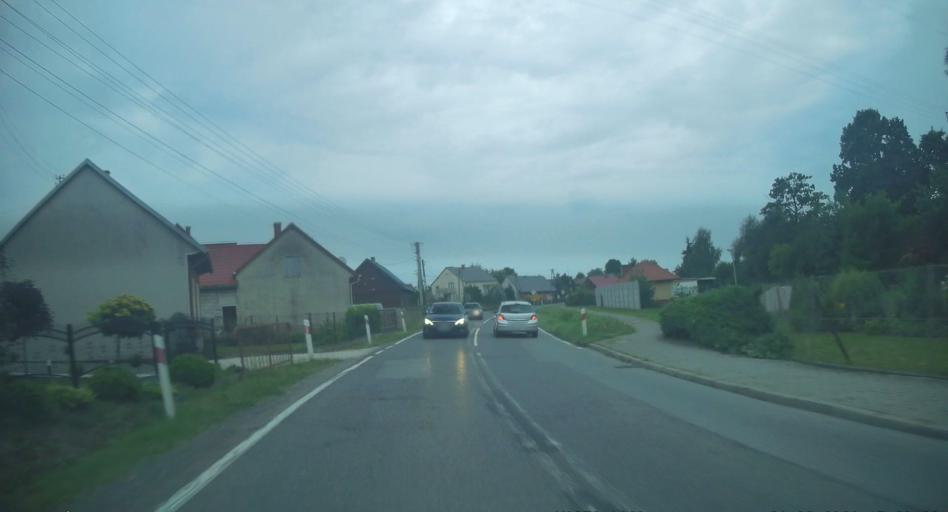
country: PL
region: Lesser Poland Voivodeship
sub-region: Powiat tarnowski
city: Wierzchoslawice
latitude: 49.9965
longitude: 20.8534
